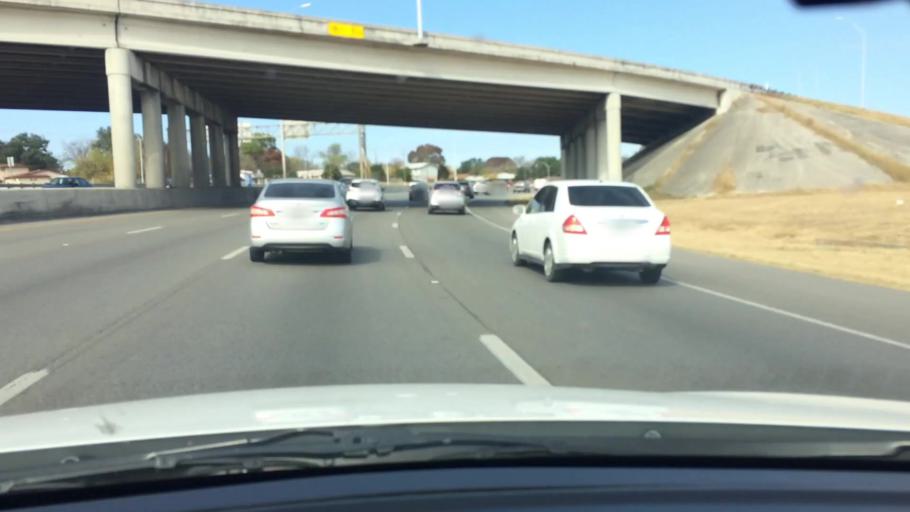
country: US
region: Texas
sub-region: Bexar County
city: Castle Hills
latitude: 29.5371
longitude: -98.4923
